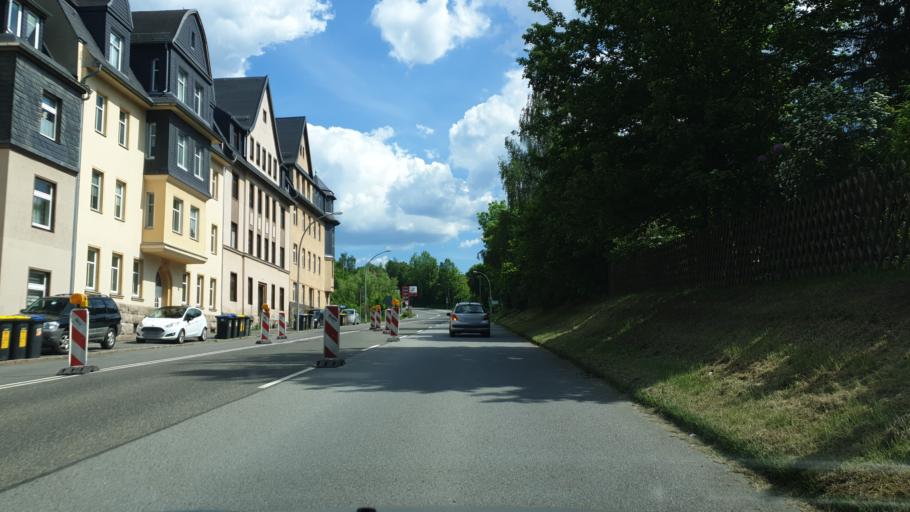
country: DE
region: Saxony
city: Aue
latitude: 50.5809
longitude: 12.7118
